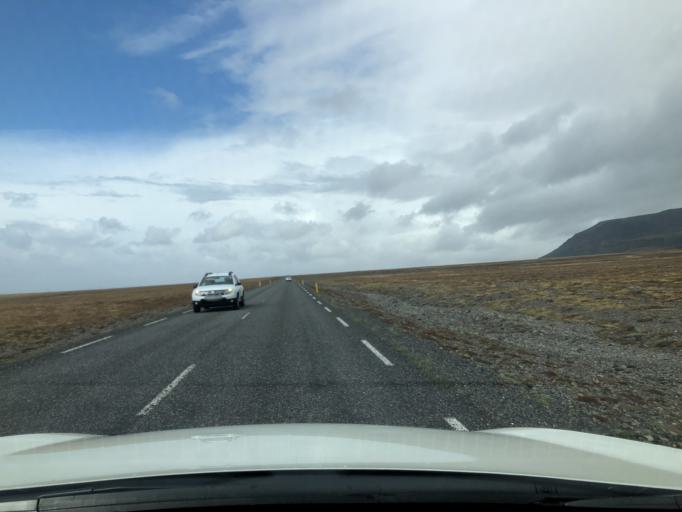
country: IS
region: East
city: Hoefn
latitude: 63.9095
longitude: -16.7312
